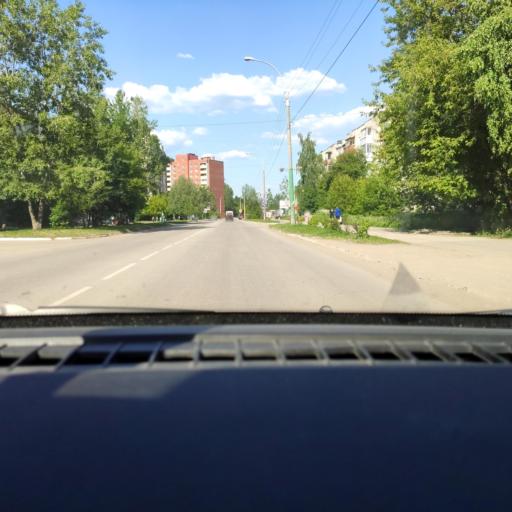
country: RU
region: Perm
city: Krasnokamsk
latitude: 58.0866
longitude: 55.7704
